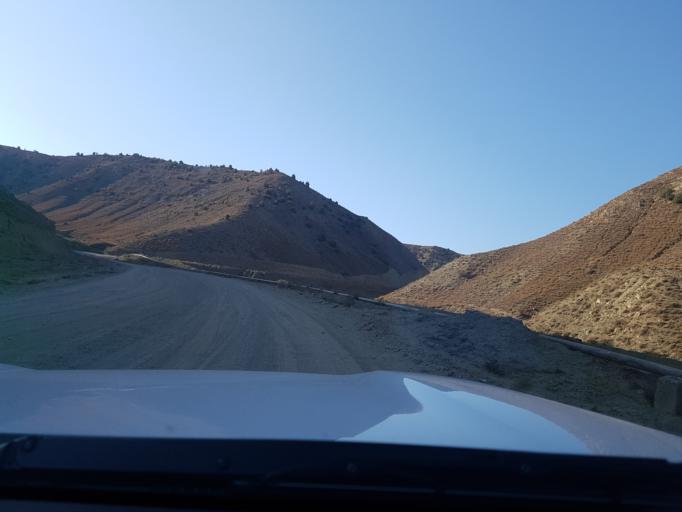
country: TM
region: Ahal
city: Baharly
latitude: 38.4473
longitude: 57.0480
